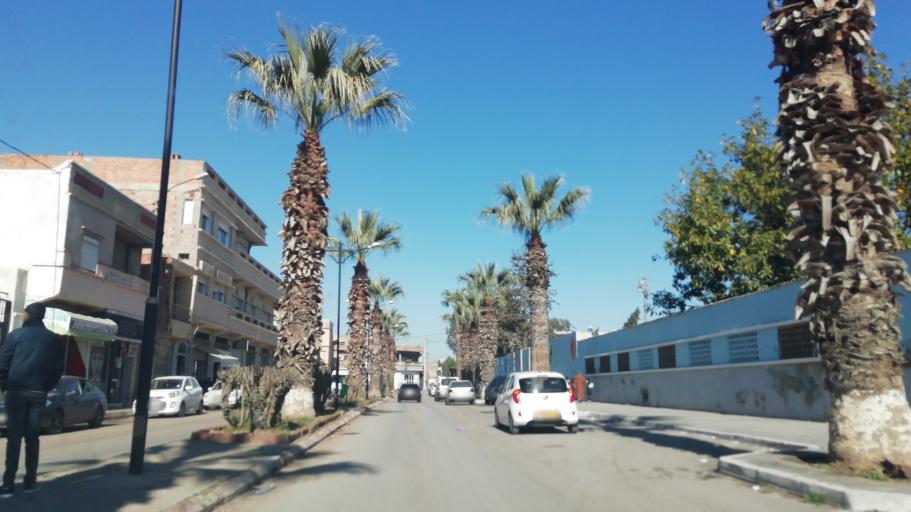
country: DZ
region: Oran
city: Es Senia
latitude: 35.6513
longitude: -0.6218
